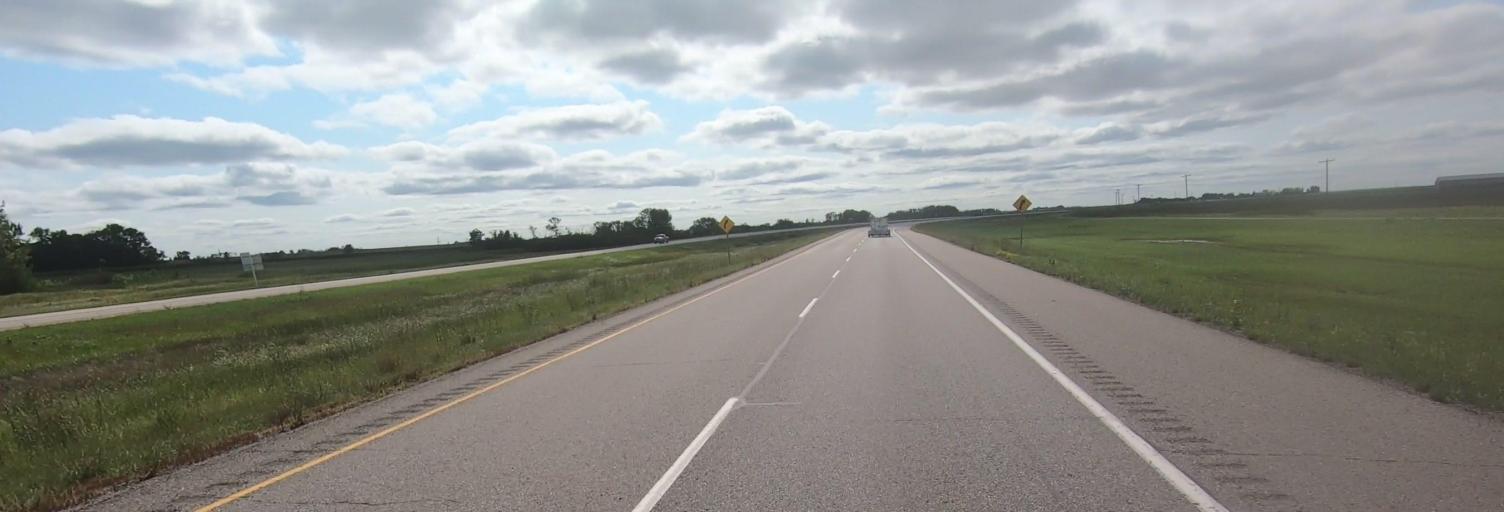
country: CA
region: Manitoba
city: Rivers
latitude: 49.8321
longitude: -100.3056
